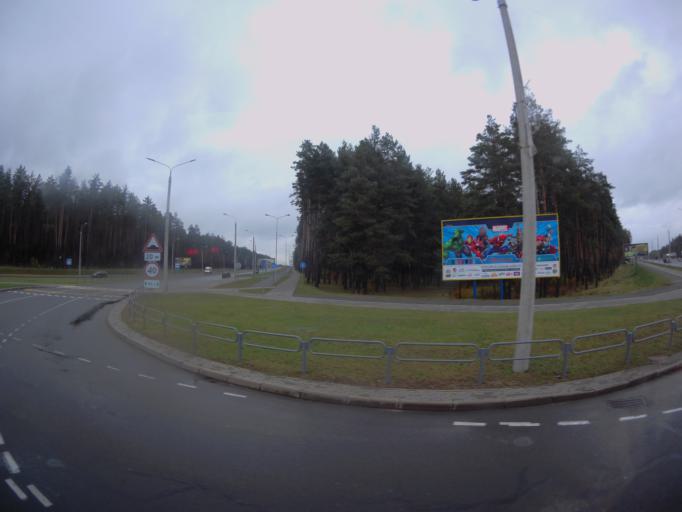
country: BY
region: Minsk
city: Horad Barysaw
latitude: 54.1966
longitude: 28.4705
